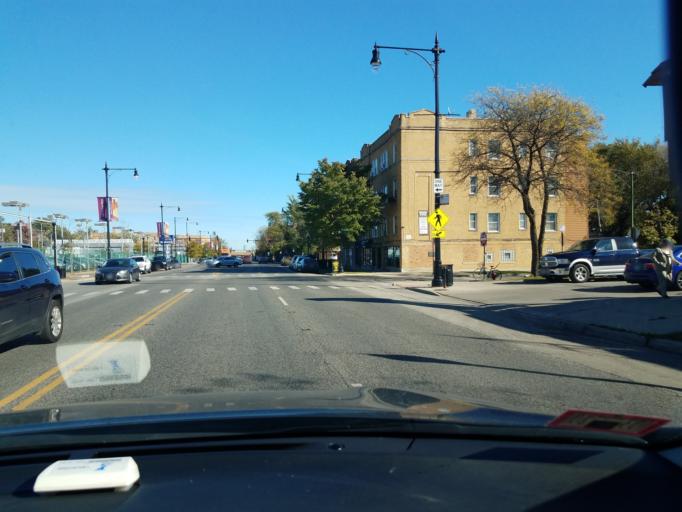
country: US
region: Illinois
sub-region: Cook County
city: Lincolnwood
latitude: 41.9535
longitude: -87.7397
